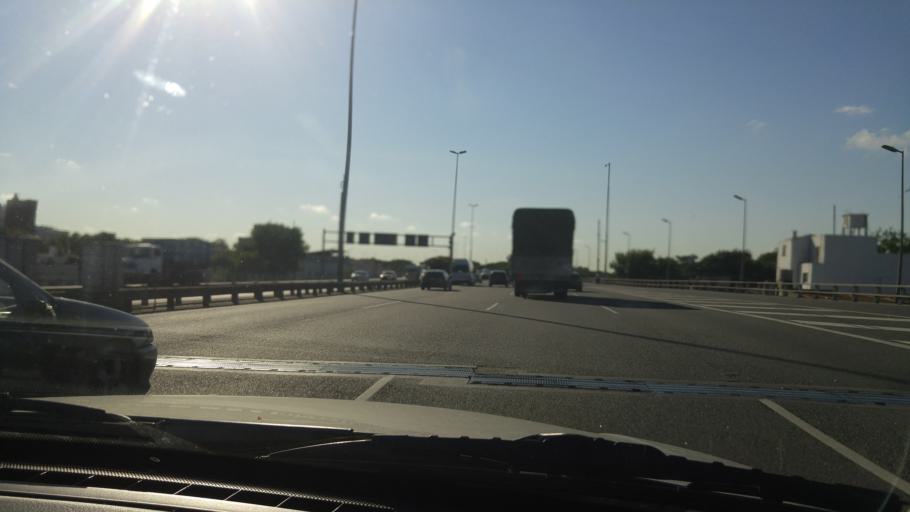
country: AR
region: Buenos Aires F.D.
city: Villa Santa Rita
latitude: -34.6439
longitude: -58.4888
